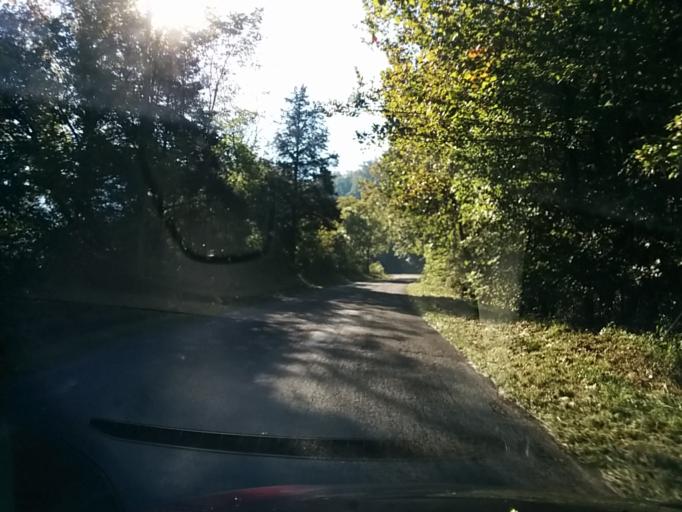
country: US
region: Virginia
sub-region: City of Lexington
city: Lexington
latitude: 37.7401
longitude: -79.5815
